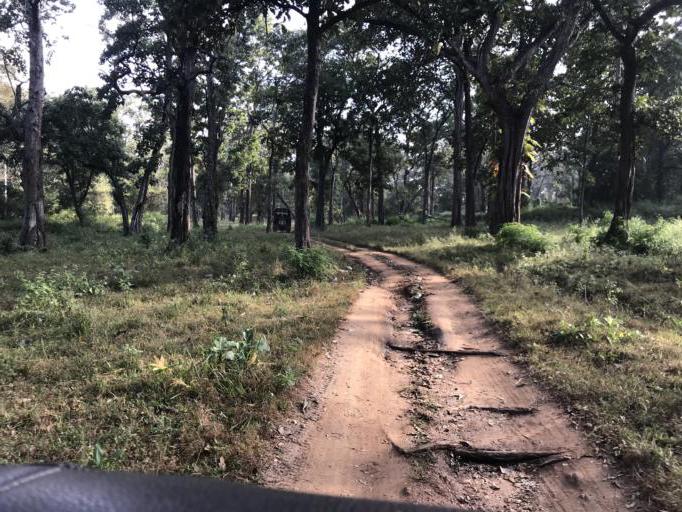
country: IN
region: Karnataka
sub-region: Mysore
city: Heggadadevankote
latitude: 11.9599
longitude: 76.2005
